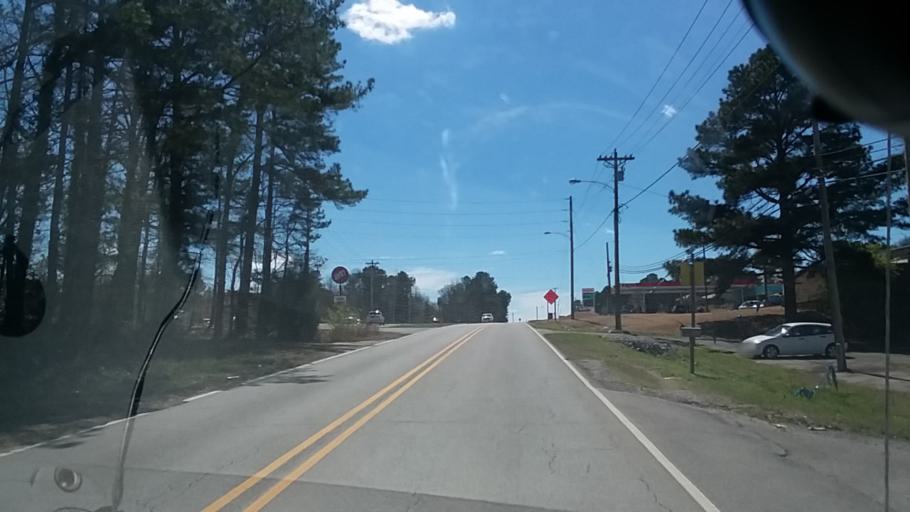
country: US
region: Mississippi
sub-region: Tishomingo County
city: Iuka
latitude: 34.7995
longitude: -88.2055
